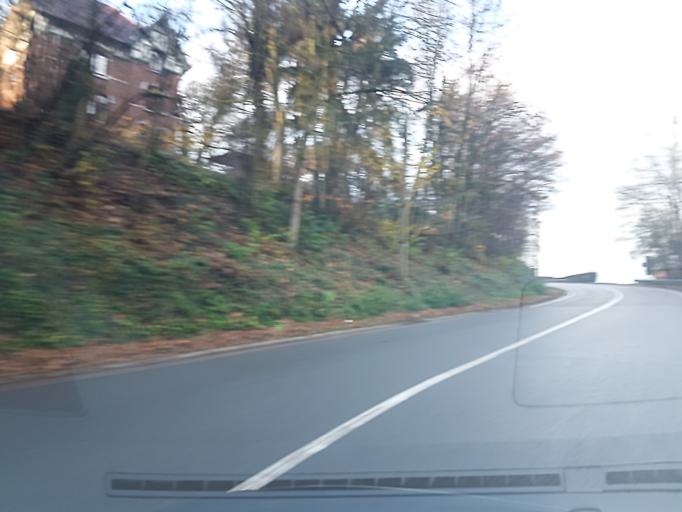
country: BE
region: Wallonia
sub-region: Province de Liege
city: Pepinster
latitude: 50.5604
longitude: 5.8116
